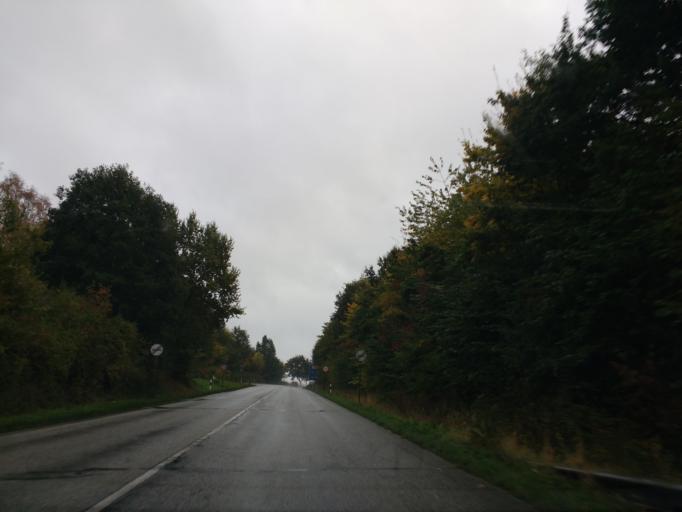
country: DE
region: Schleswig-Holstein
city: Susel
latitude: 54.0586
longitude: 10.7249
